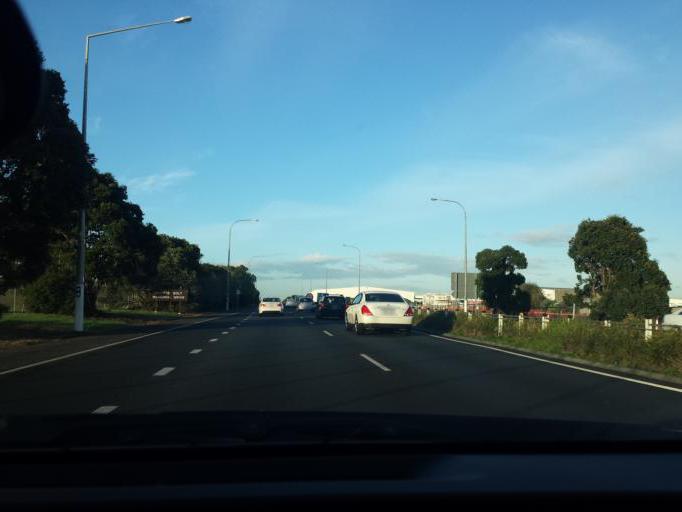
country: NZ
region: Auckland
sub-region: Auckland
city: Mangere
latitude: -36.9752
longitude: 174.7885
